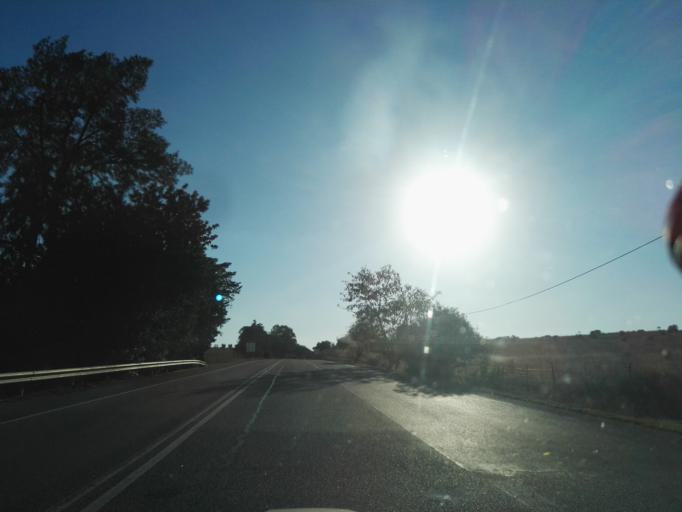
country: PT
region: Evora
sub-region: Vila Vicosa
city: Vila Vicosa
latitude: 38.8511
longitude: -7.3360
